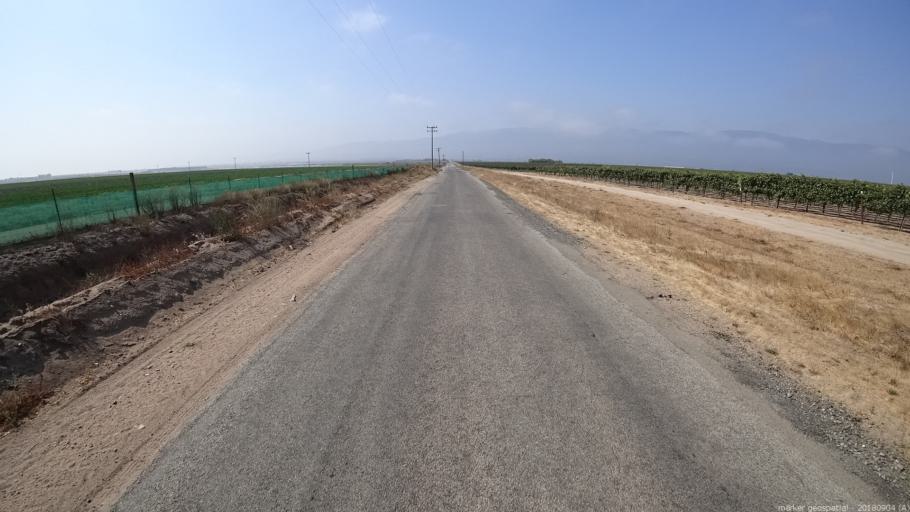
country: US
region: California
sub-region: Monterey County
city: Soledad
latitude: 36.4726
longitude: -121.3499
